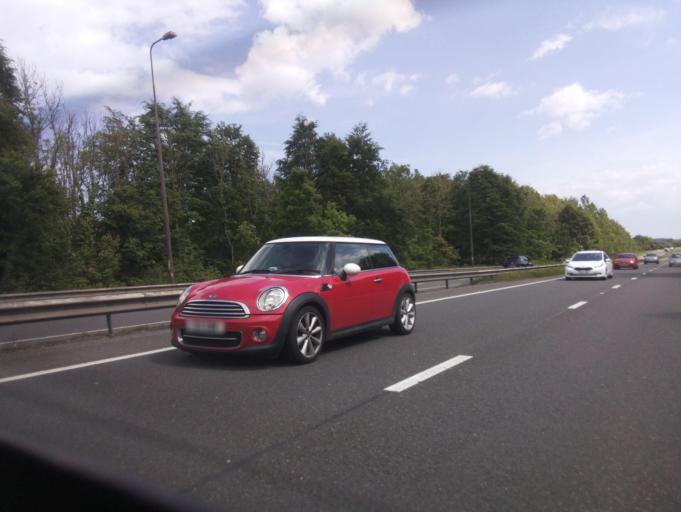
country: GB
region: England
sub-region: County Durham
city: Peterlee
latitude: 54.7273
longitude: -1.3411
